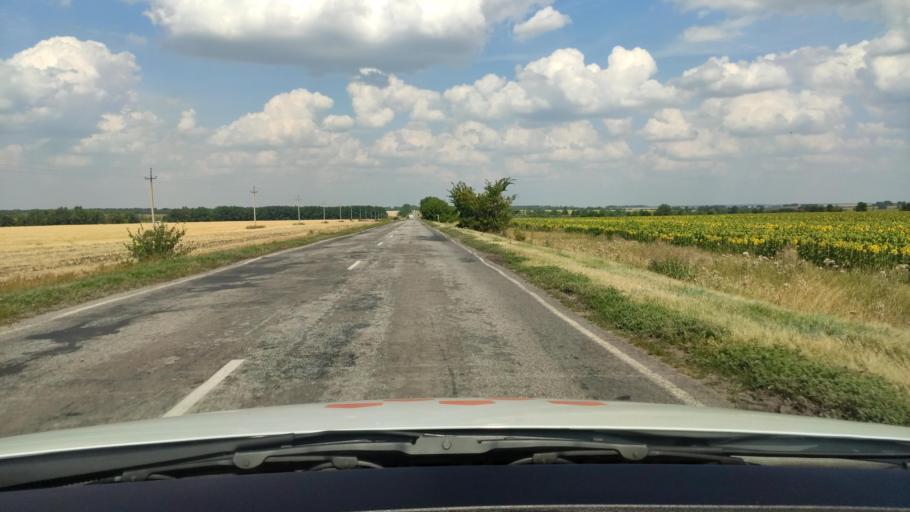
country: RU
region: Voronezj
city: Pereleshinskiy
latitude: 51.7396
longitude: 40.3958
